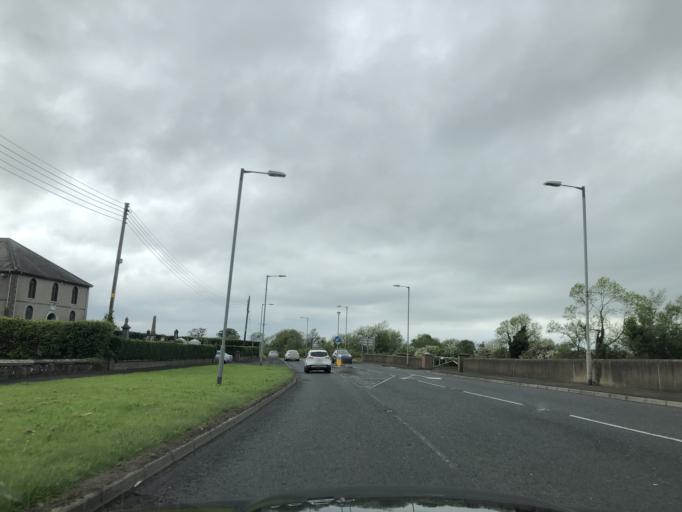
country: GB
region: Northern Ireland
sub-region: Antrim Borough
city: Templepatrick
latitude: 54.6149
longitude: -6.1200
